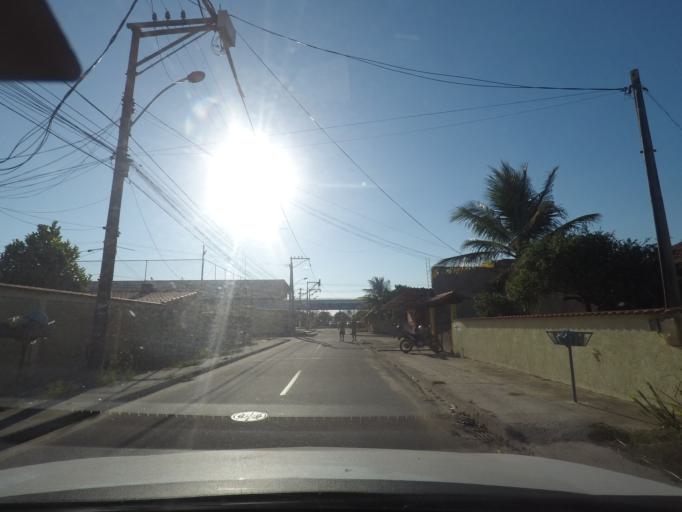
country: BR
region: Rio de Janeiro
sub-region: Marica
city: Marica
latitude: -22.9621
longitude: -42.9608
